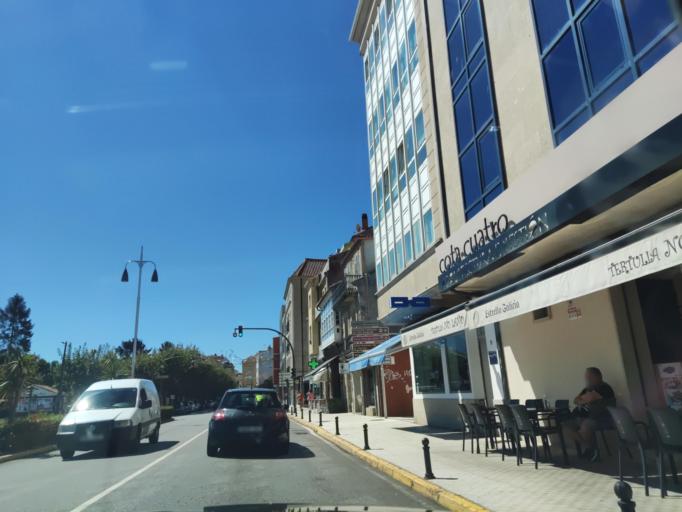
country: ES
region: Galicia
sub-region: Provincia da Coruna
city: Boiro
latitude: 42.6067
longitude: -8.9381
